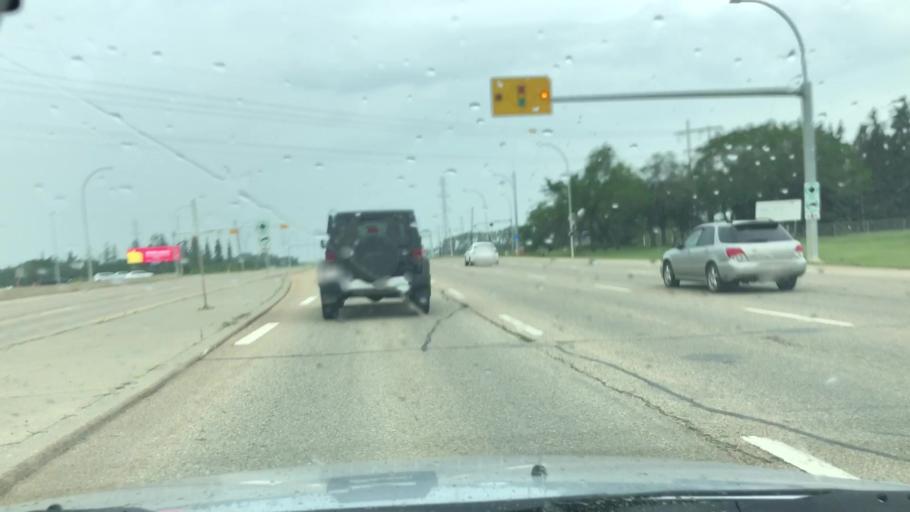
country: CA
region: Alberta
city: St. Albert
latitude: 53.6108
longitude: -113.5896
